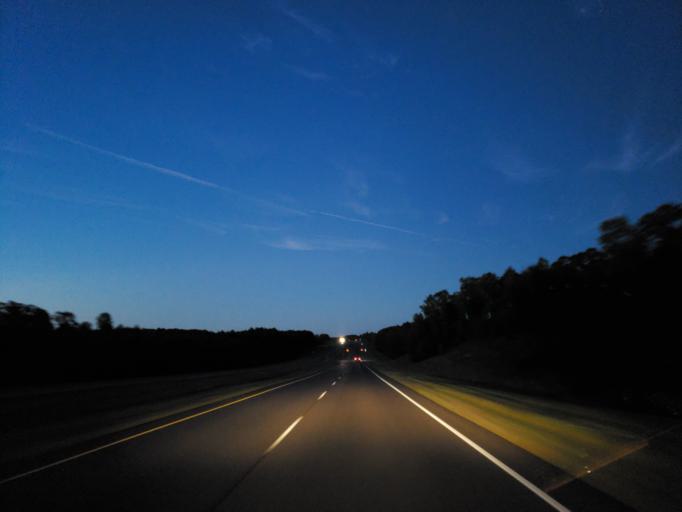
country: US
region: Mississippi
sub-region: Clarke County
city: Quitman
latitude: 32.0311
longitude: -88.6815
